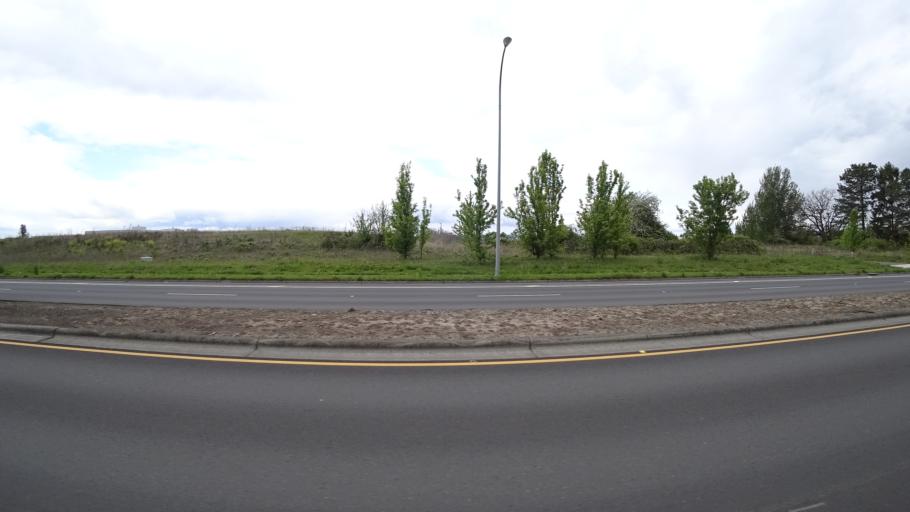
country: US
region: Oregon
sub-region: Washington County
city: Rockcreek
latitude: 45.5509
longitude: -122.9234
